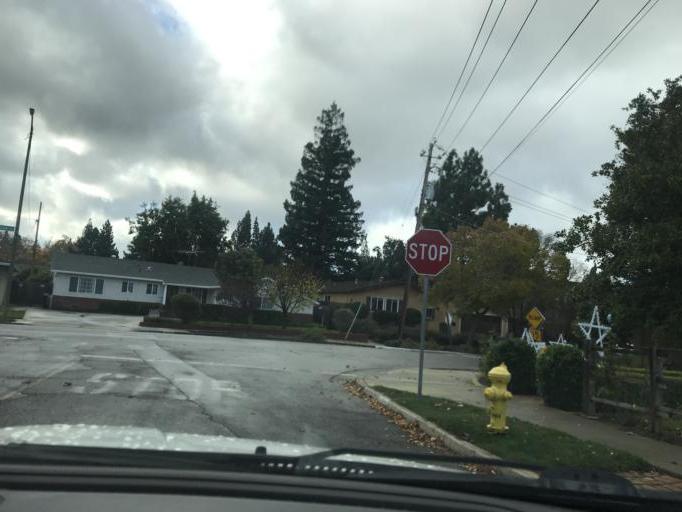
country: US
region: California
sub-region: Santa Clara County
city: Buena Vista
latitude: 37.2952
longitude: -121.9077
